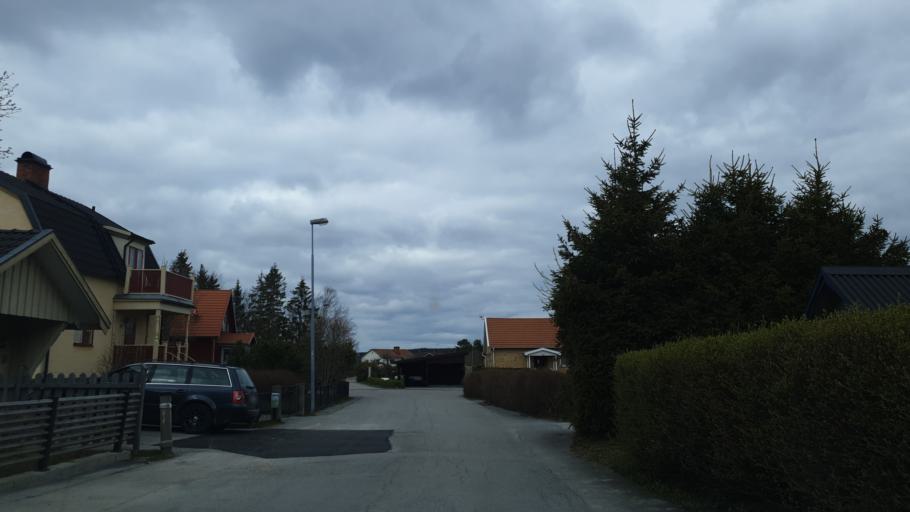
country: SE
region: OErebro
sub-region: Nora Kommun
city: Nora
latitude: 59.5254
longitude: 15.0405
